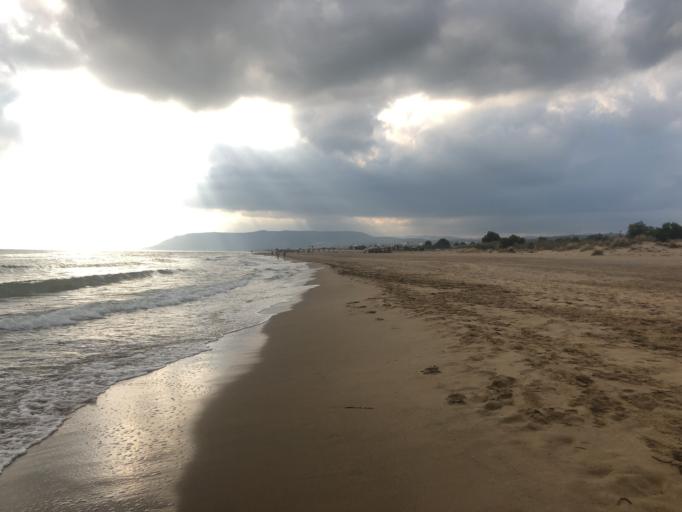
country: GR
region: Crete
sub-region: Nomos Chanias
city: Georgioupolis
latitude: 35.3559
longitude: 24.2827
